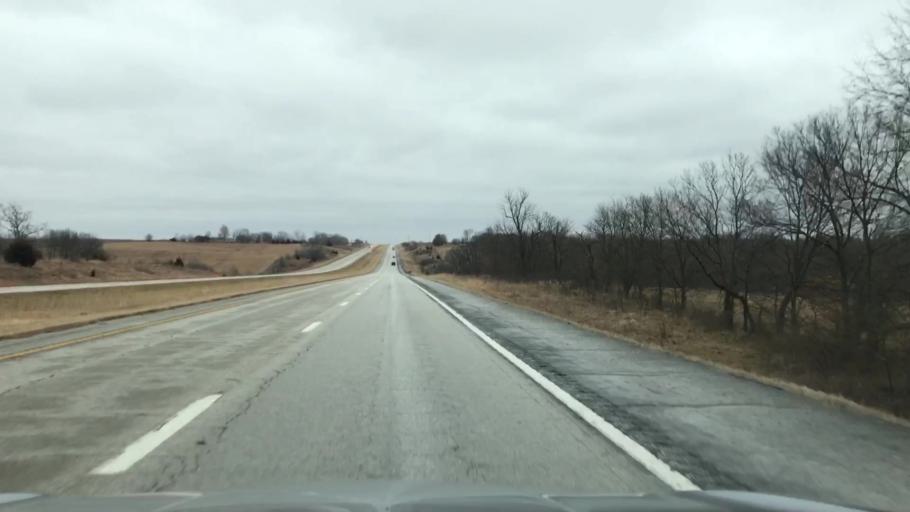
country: US
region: Missouri
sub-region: Caldwell County
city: Hamilton
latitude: 39.7499
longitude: -94.1022
